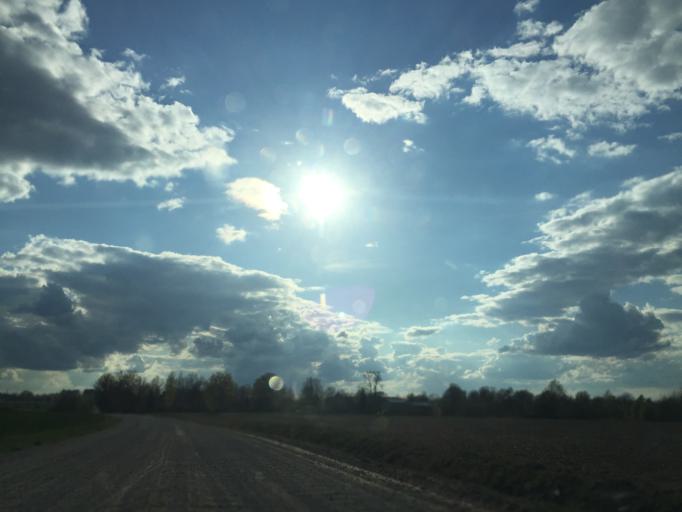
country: LV
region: Beverina
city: Murmuiza
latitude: 57.3974
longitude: 25.4648
